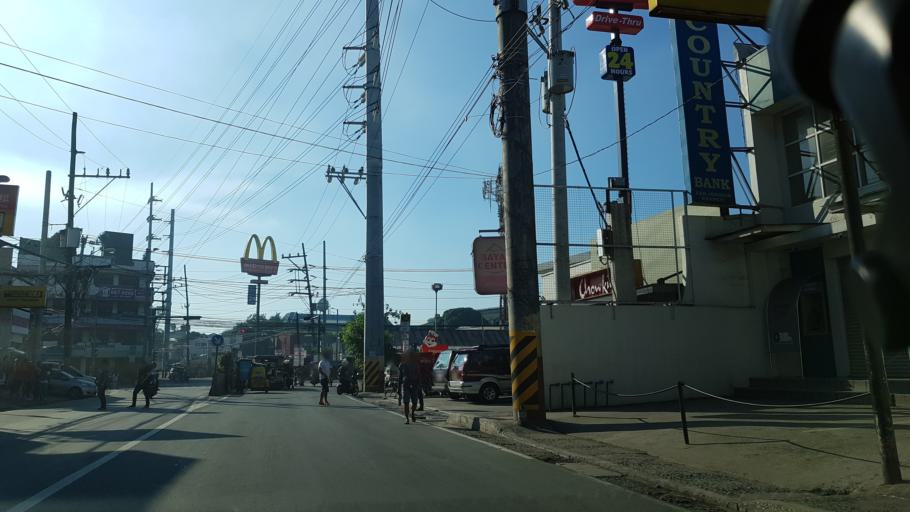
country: PH
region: Calabarzon
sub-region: Province of Rizal
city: Pateros
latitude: 14.5521
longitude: 121.0740
